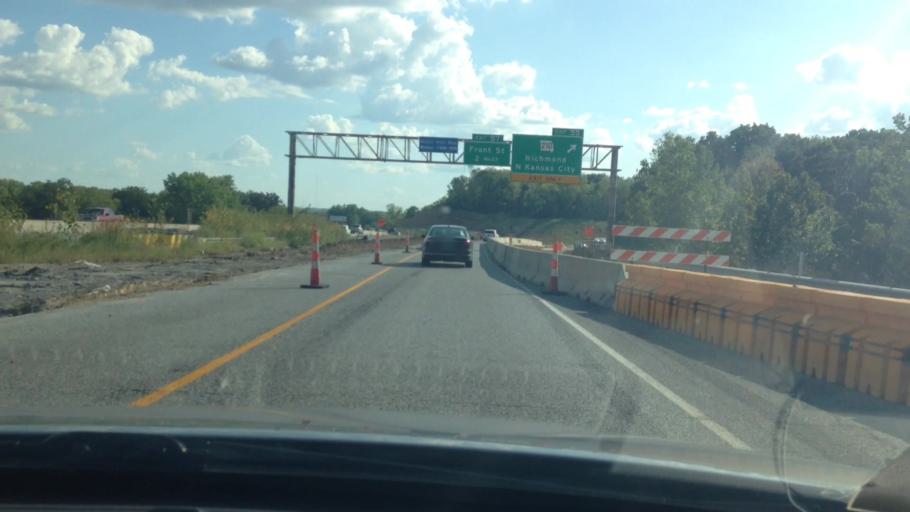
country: US
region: Missouri
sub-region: Clay County
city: Claycomo
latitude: 39.1616
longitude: -94.4966
